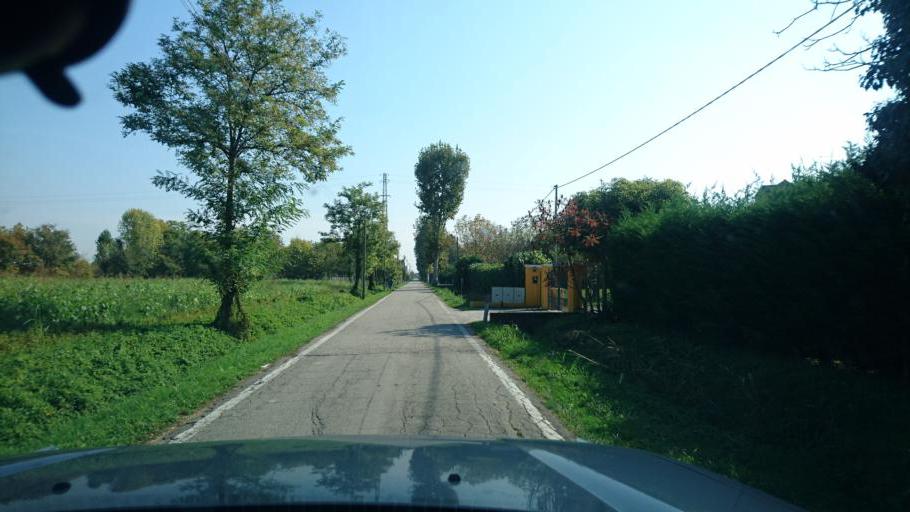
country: IT
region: Veneto
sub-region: Provincia di Padova
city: Rubano
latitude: 45.4122
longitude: 11.7884
